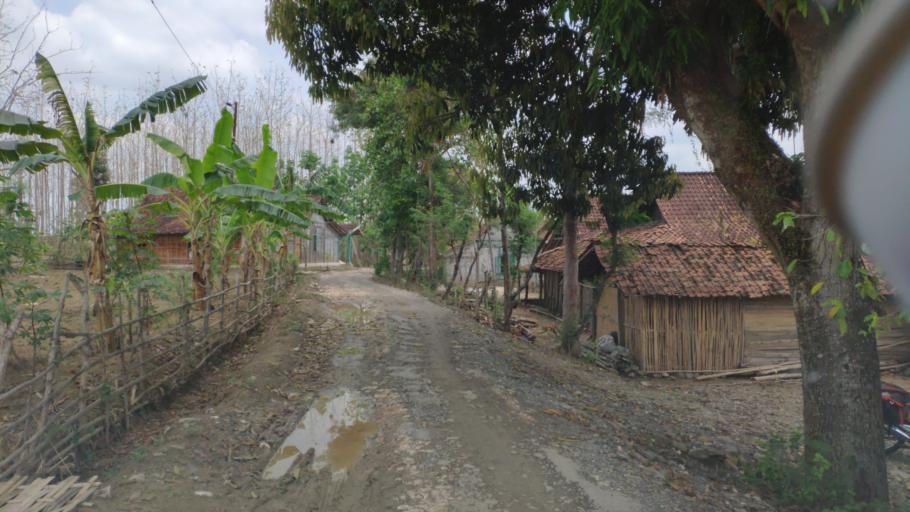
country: ID
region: Central Java
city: Gumiring
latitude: -7.0447
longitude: 111.3919
